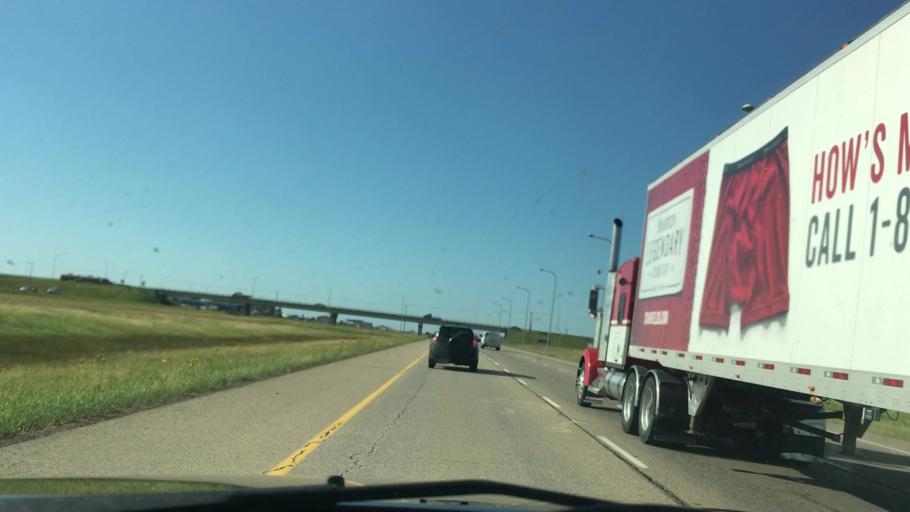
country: CA
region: Alberta
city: Leduc
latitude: 53.3130
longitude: -113.5501
